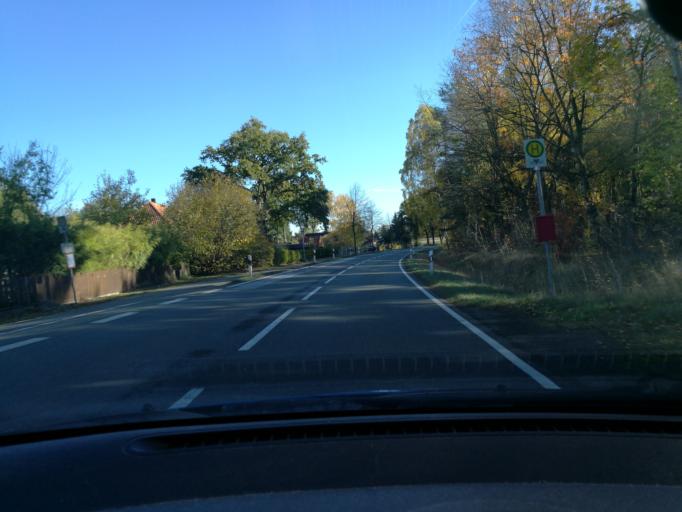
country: DE
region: Lower Saxony
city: Karwitz
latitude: 53.1050
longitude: 11.0442
